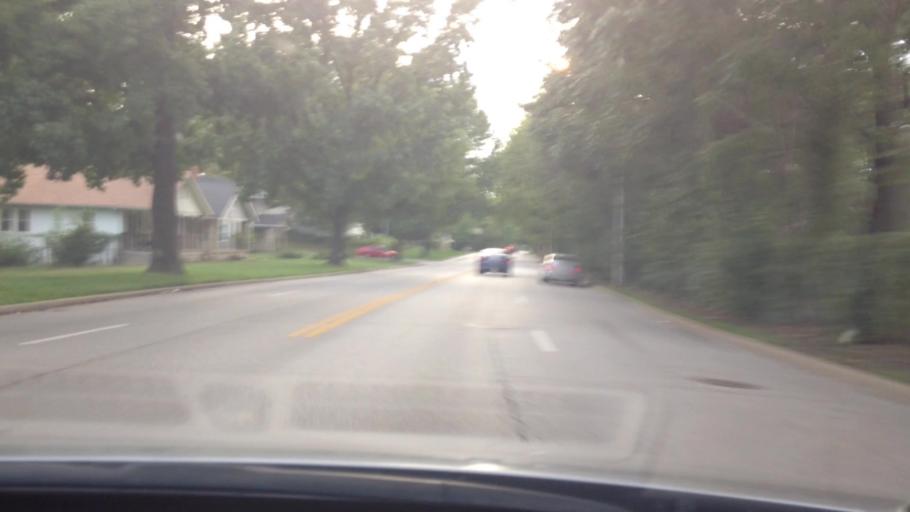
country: US
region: Kansas
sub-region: Johnson County
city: Mission Hills
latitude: 38.9984
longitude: -94.5661
